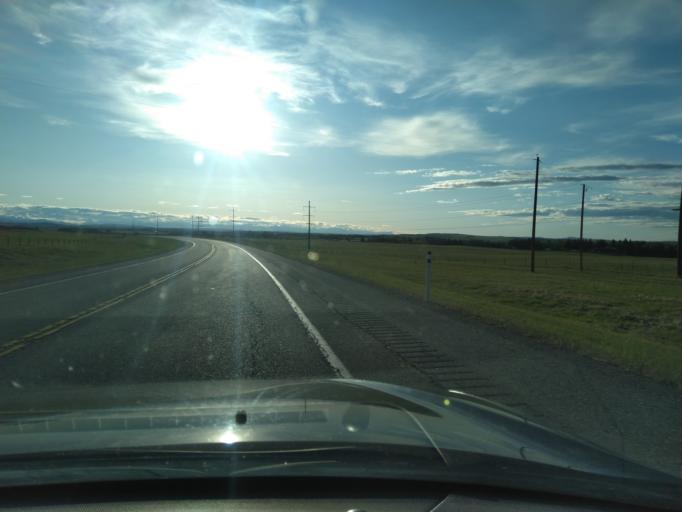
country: CA
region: Alberta
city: Cochrane
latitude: 51.0228
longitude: -114.3318
